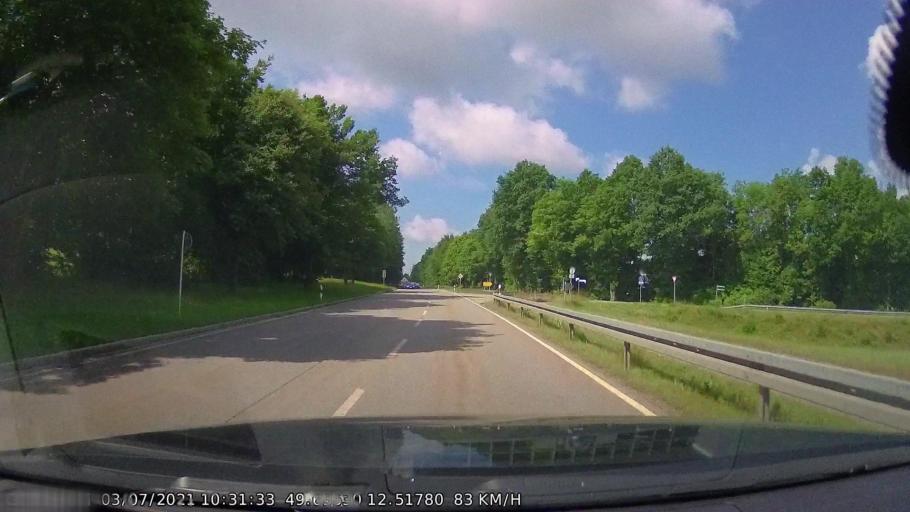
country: DE
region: Bavaria
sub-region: Upper Palatinate
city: Waidhaus
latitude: 49.6552
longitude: 12.5177
